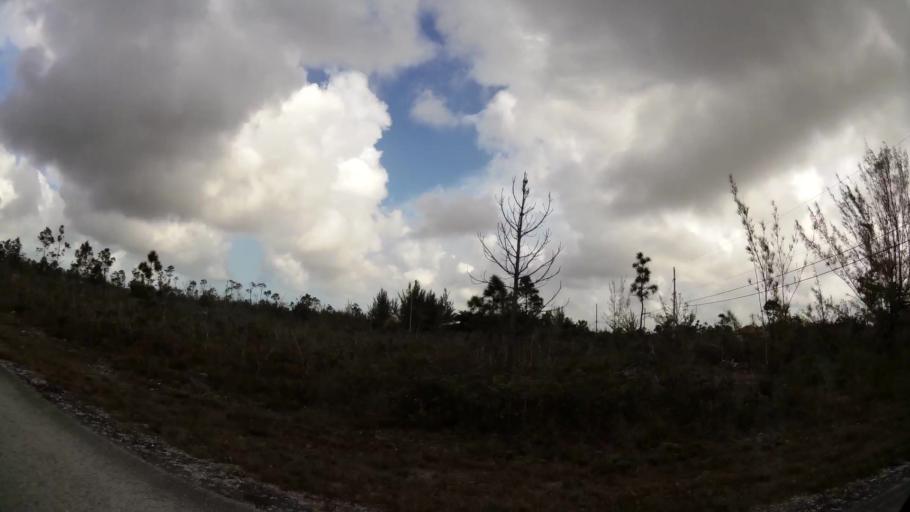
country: BS
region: Freeport
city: Lucaya
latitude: 26.5786
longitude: -78.5812
